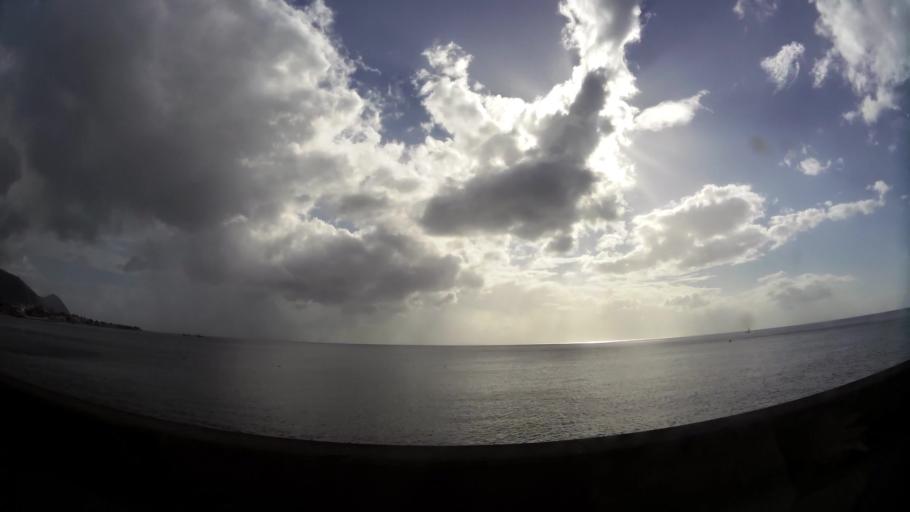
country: DM
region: Saint George
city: Roseau
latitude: 15.3188
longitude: -61.3925
